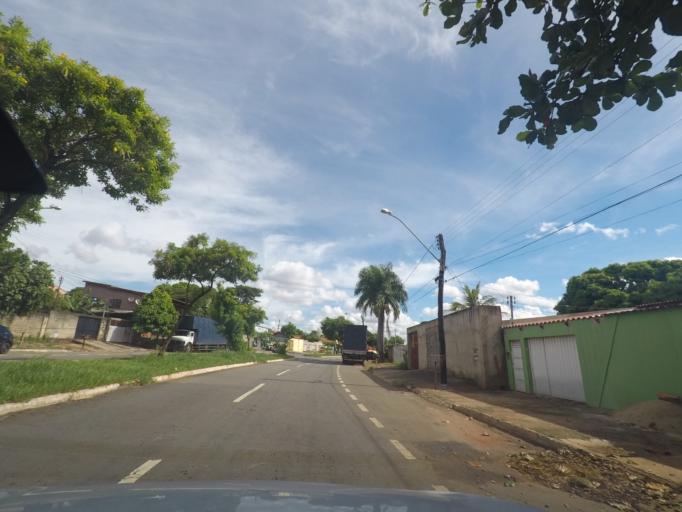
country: BR
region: Goias
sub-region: Goiania
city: Goiania
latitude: -16.7052
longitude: -49.3172
